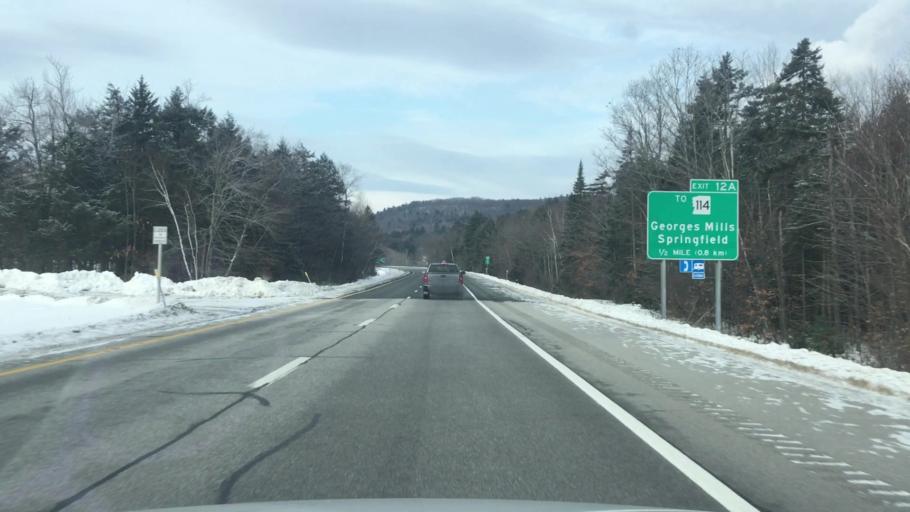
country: US
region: New Hampshire
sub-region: Sullivan County
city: Springfield
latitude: 43.4389
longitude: -72.0510
